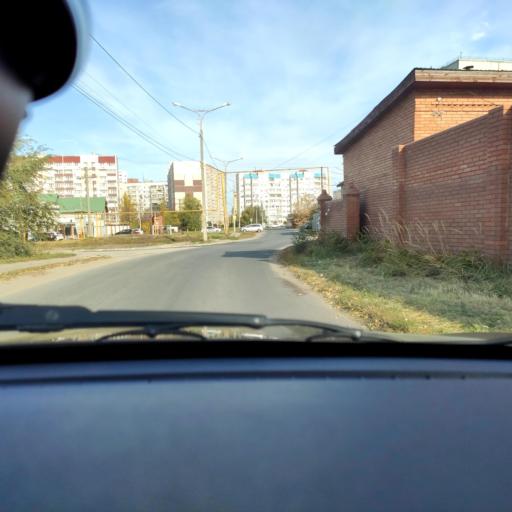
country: RU
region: Samara
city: Tol'yatti
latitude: 53.5370
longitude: 49.3968
